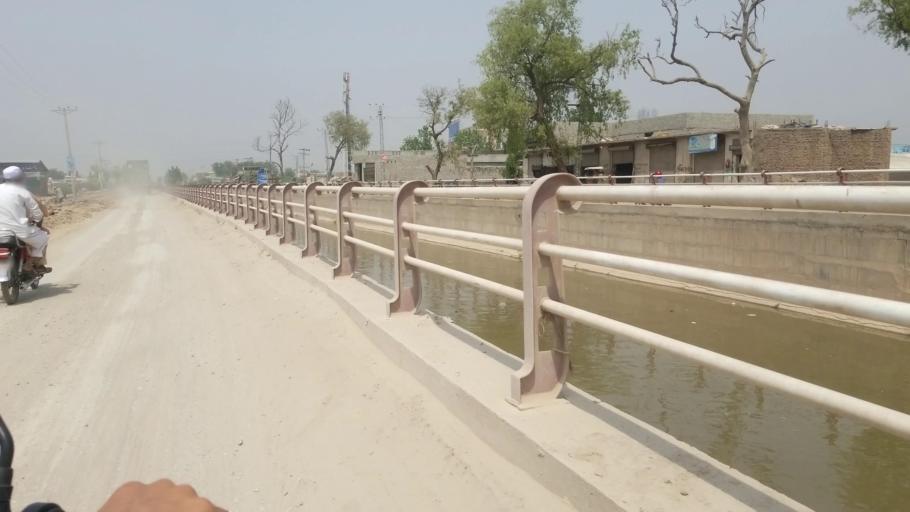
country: PK
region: Khyber Pakhtunkhwa
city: Peshawar
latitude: 33.9672
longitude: 71.5406
